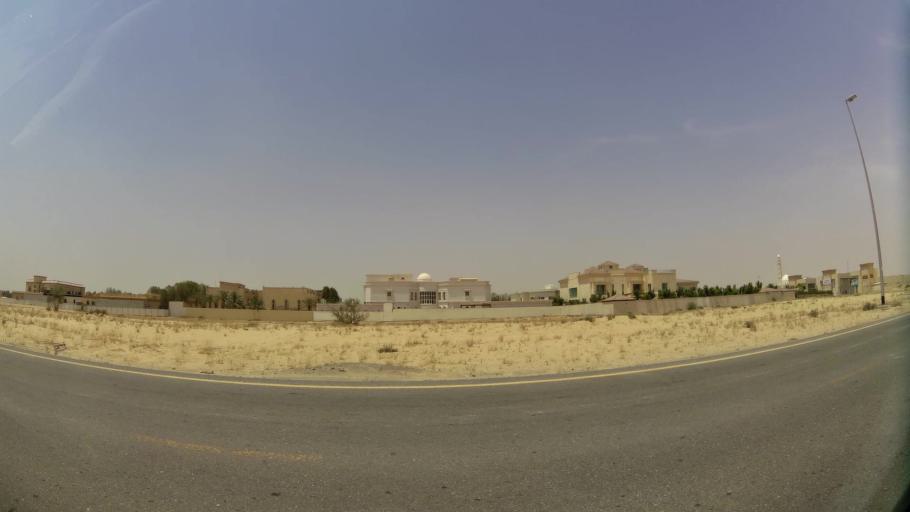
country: AE
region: Ash Shariqah
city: Sharjah
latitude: 25.2480
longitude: 55.4778
